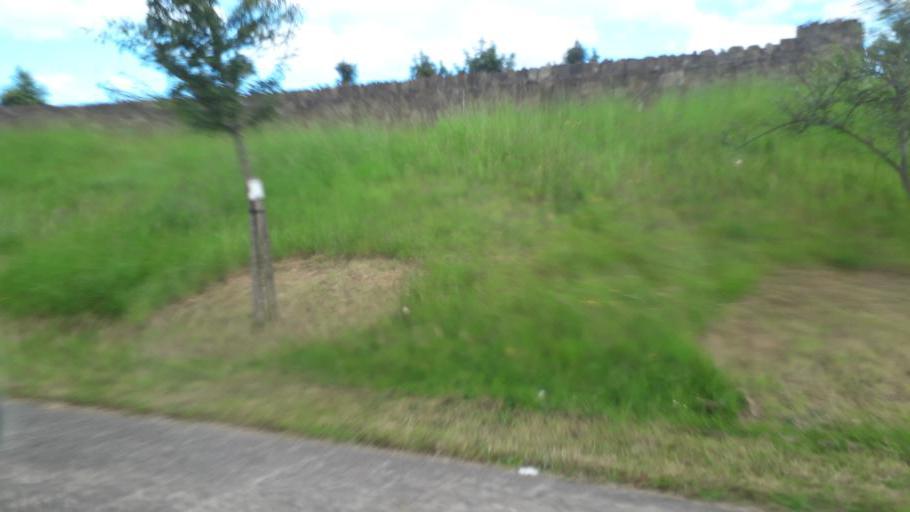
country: IE
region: Leinster
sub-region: Loch Garman
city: Gorey
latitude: 52.6797
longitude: -6.2850
